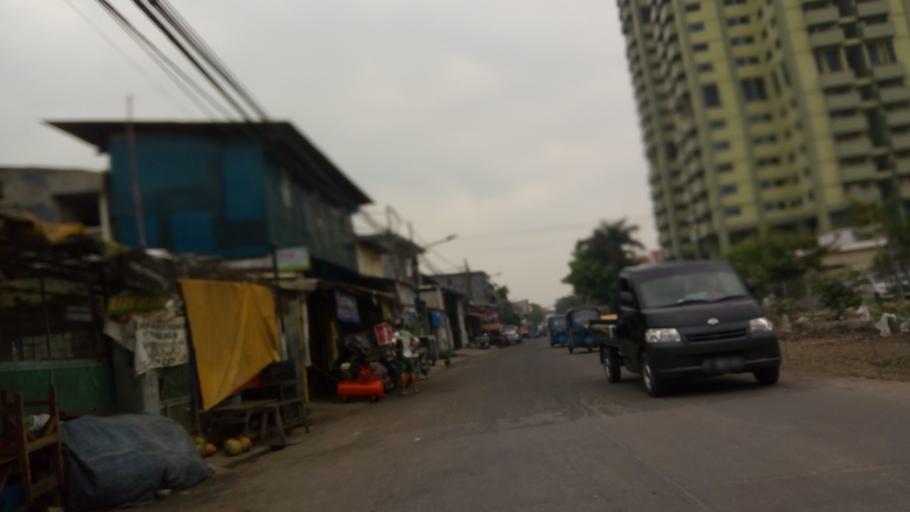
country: ID
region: Jakarta Raya
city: Jakarta
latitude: -6.1455
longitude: 106.8375
